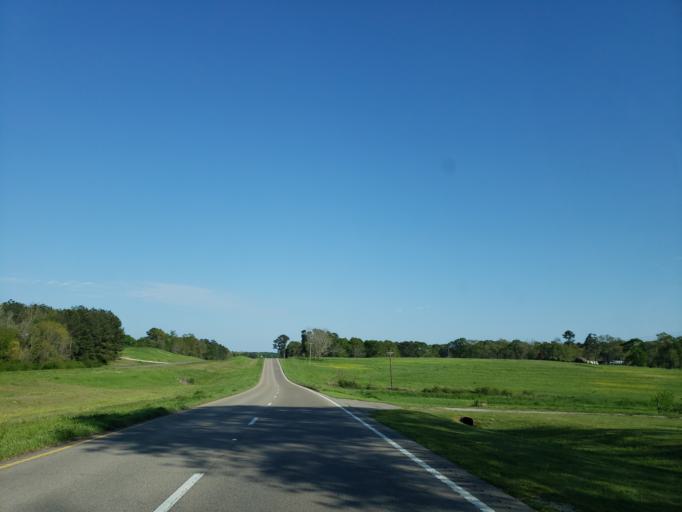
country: US
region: Mississippi
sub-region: Jones County
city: Ellisville
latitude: 31.6884
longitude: -89.3274
